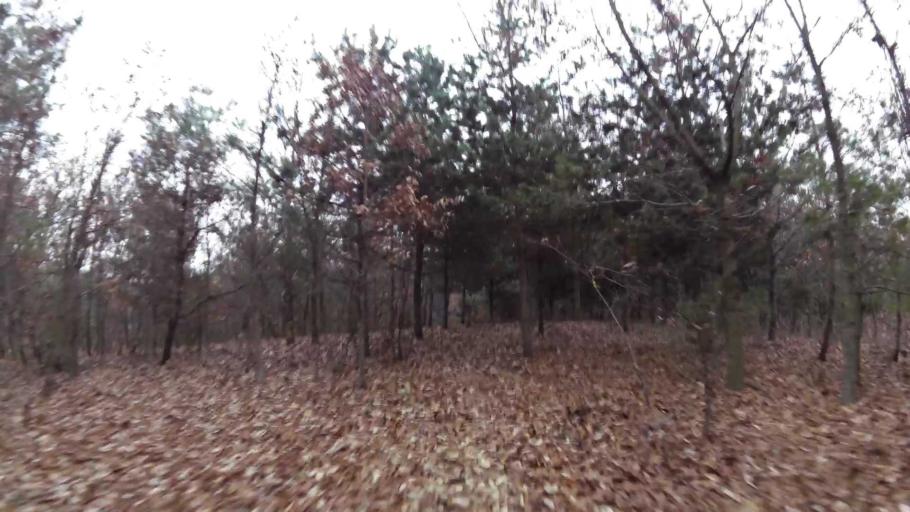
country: KR
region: Daegu
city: Daegu
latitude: 35.8609
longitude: 128.6679
